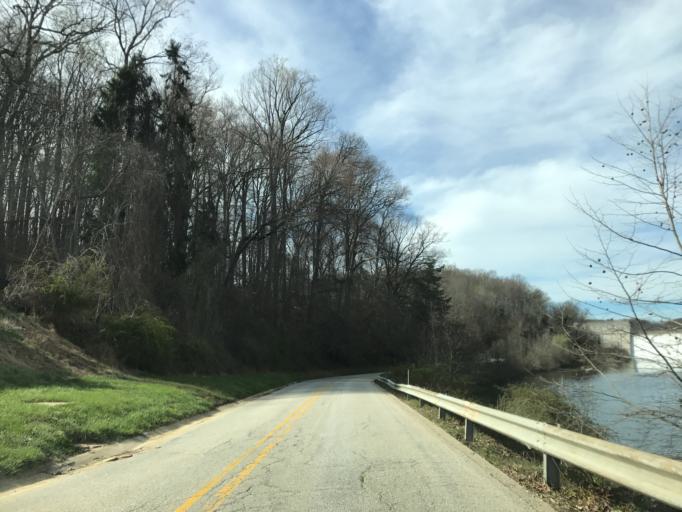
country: US
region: Maryland
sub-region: Baltimore County
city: Carney
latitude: 39.4262
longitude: -76.5446
